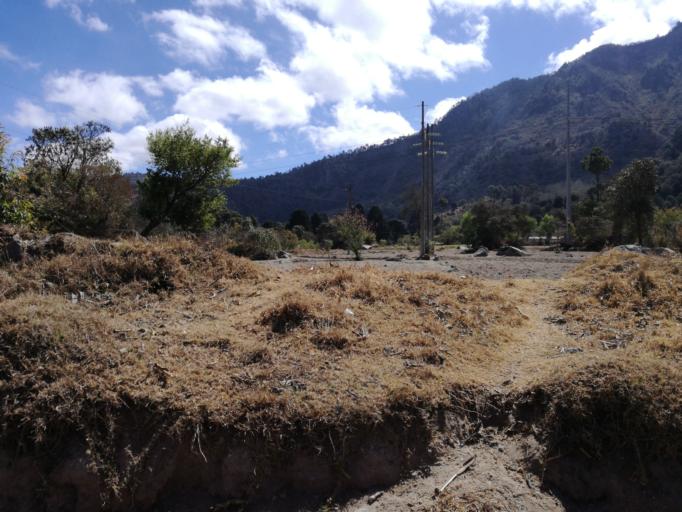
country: GT
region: Quetzaltenango
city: Quetzaltenango
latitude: 14.8008
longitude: -91.5381
